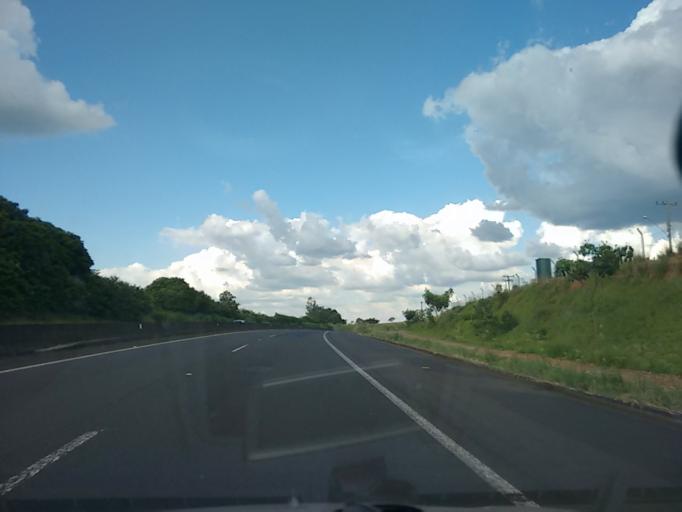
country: BR
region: Sao Paulo
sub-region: Marilia
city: Marilia
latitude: -22.2271
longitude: -49.8046
